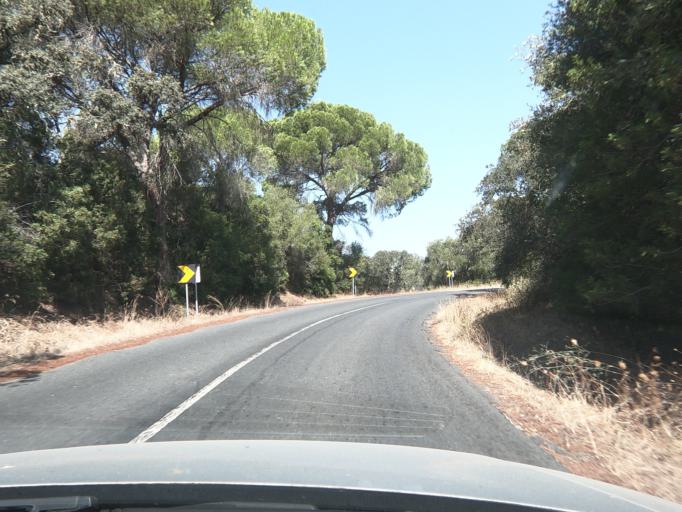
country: PT
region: Setubal
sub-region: Alcacer do Sal
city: Alcacer do Sal
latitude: 38.2898
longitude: -8.4044
